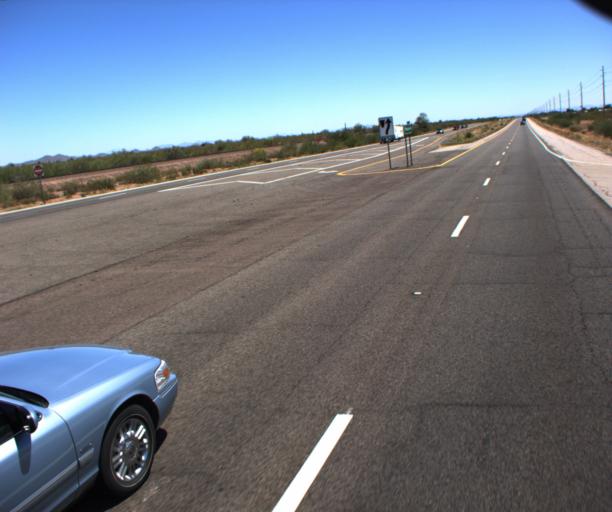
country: US
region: Arizona
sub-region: Maricopa County
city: Wickenburg
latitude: 33.7968
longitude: -112.5532
